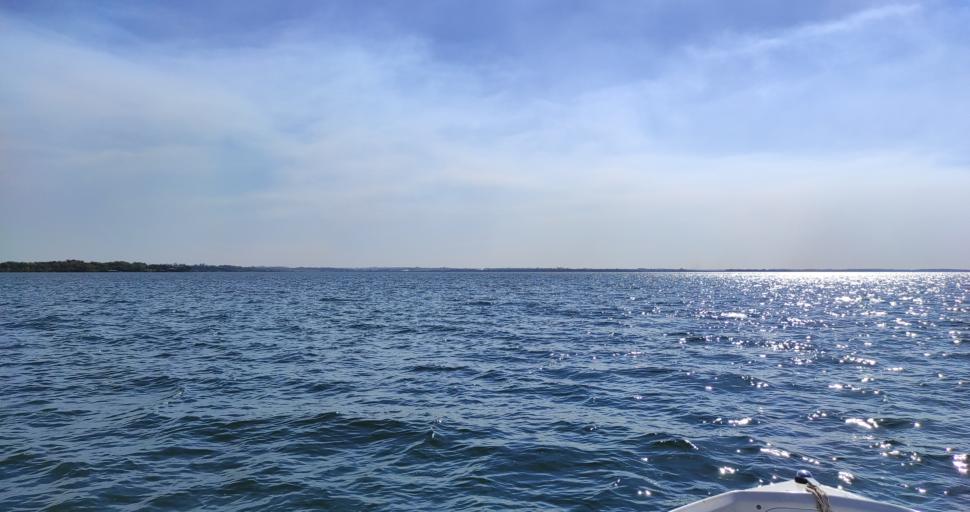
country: AR
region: Misiones
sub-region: Departamento de Capital
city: Posadas
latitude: -27.3437
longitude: -55.9385
